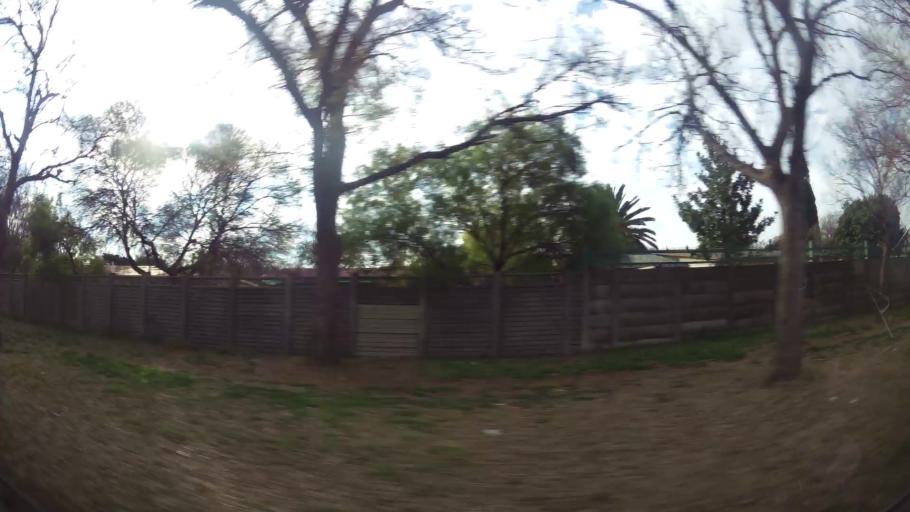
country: ZA
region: Orange Free State
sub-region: Fezile Dabi District Municipality
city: Sasolburg
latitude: -26.8181
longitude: 27.8159
